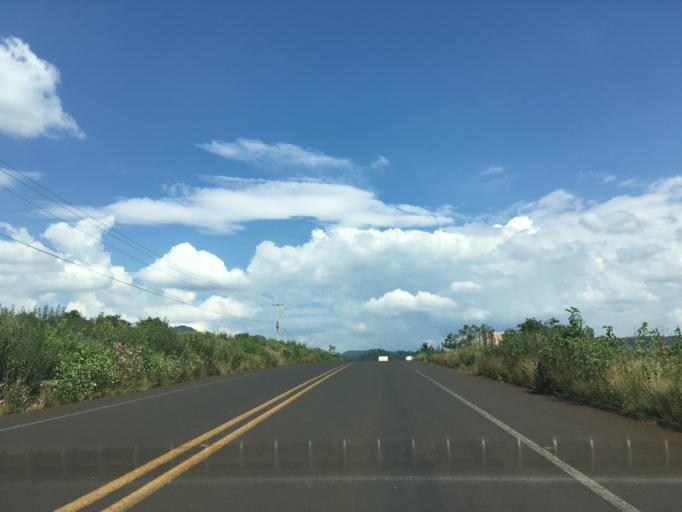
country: MX
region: Michoacan
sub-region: Tingueindin
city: Tingueindin
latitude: 19.8392
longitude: -102.4894
